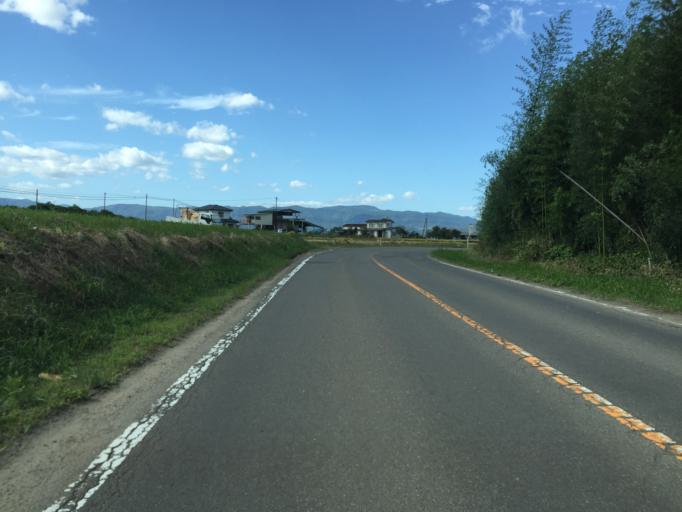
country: JP
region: Fukushima
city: Yanagawamachi-saiwaicho
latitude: 37.8406
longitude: 140.6147
